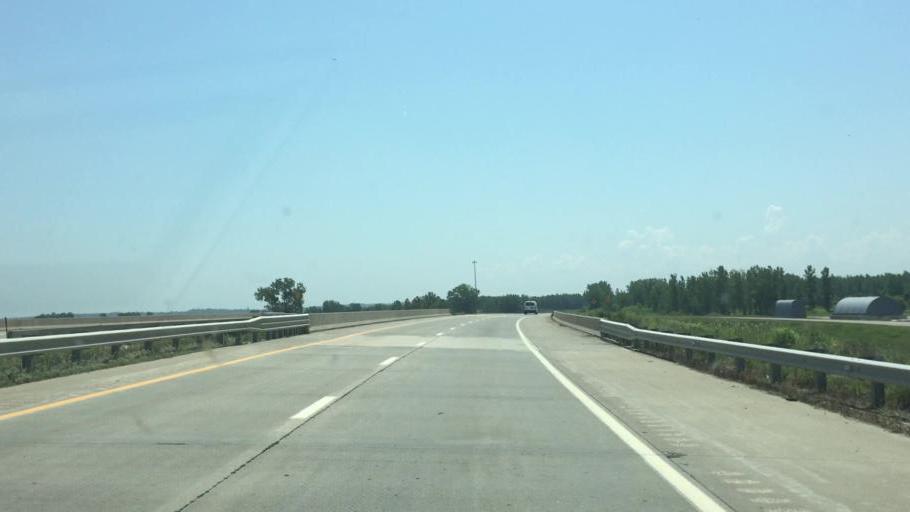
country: US
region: Kansas
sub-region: Doniphan County
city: Wathena
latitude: 39.7476
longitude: -94.9256
